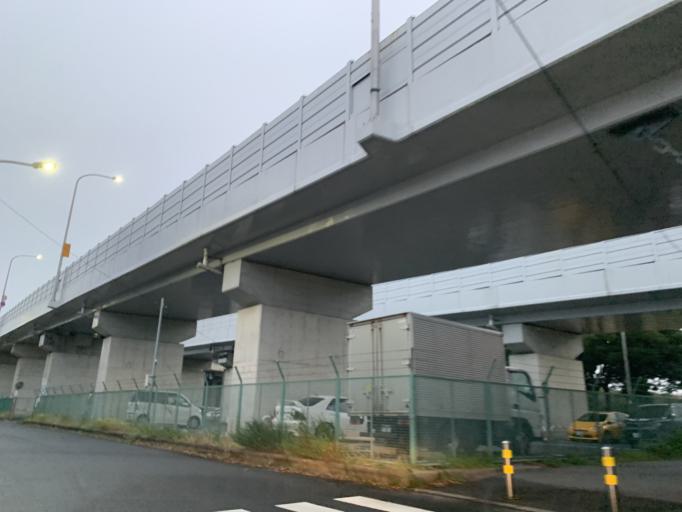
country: JP
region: Chiba
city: Funabashi
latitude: 35.6608
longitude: 140.0336
